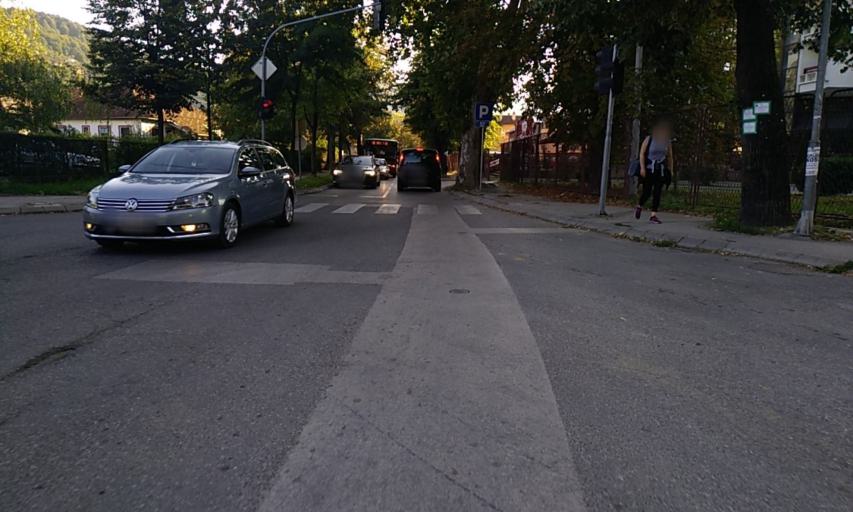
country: BA
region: Republika Srpska
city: Hiseti
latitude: 44.7598
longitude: 17.1847
